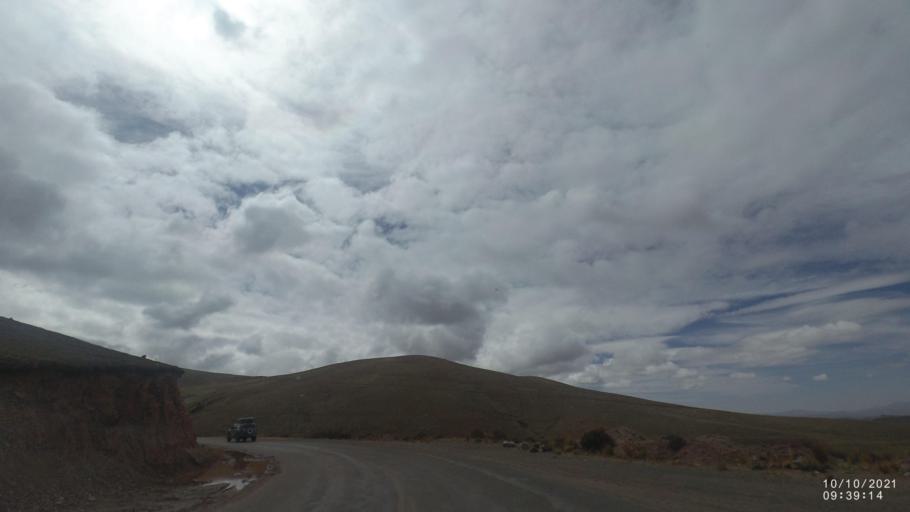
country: BO
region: La Paz
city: Quime
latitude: -17.1371
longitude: -67.3421
